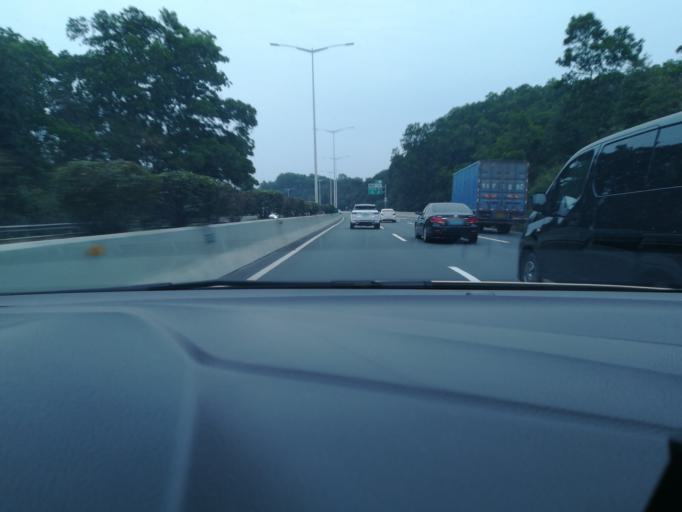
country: CN
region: Guangdong
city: Taihe
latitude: 23.2681
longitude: 113.3618
